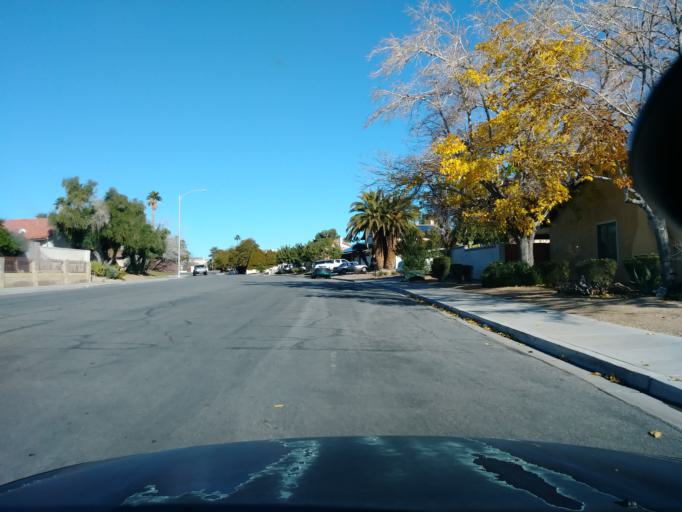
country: US
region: Nevada
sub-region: Clark County
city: Spring Valley
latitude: 36.1480
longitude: -115.2297
